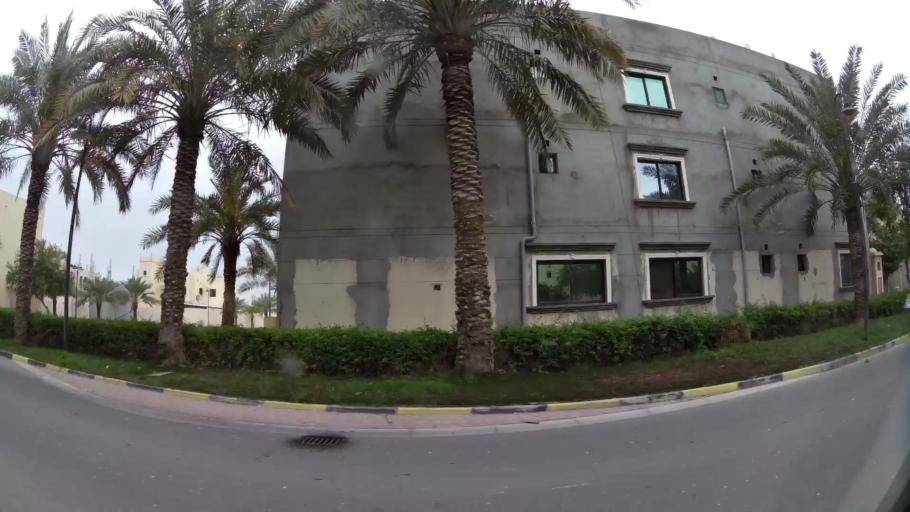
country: BH
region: Northern
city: Madinat `Isa
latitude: 26.1728
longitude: 50.5371
